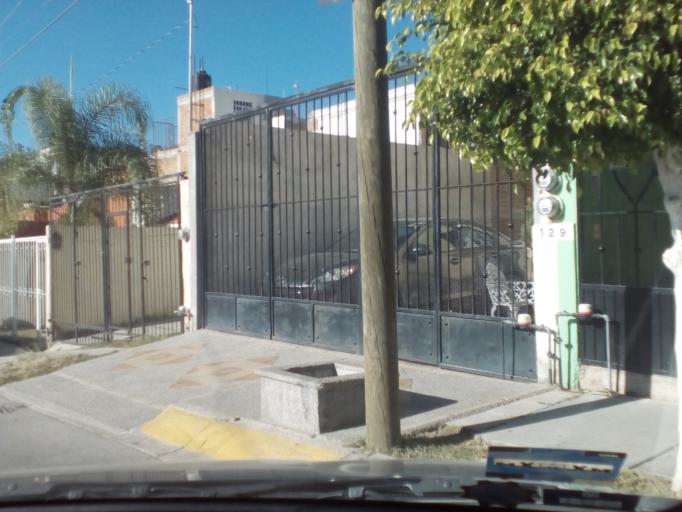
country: MX
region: Guanajuato
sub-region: Leon
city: Ejido la Joya
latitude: 21.1290
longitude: -101.7151
